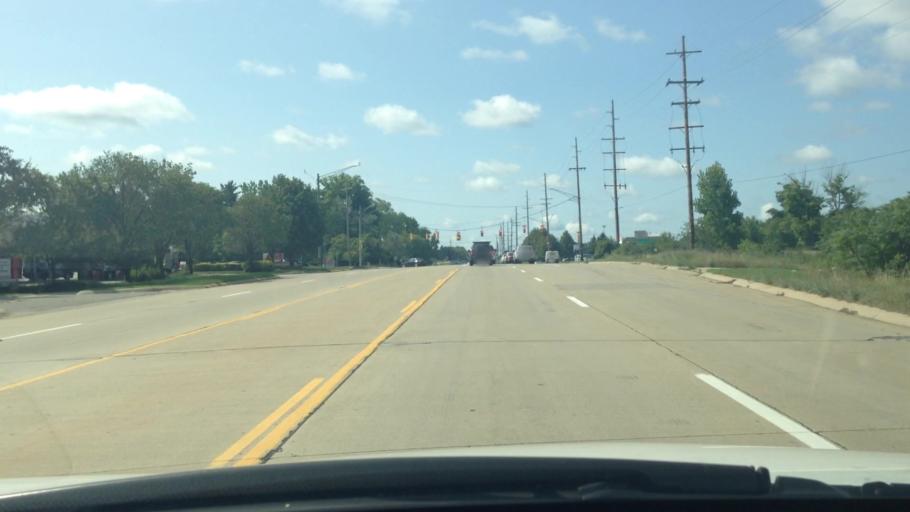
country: US
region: Michigan
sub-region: Oakland County
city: Wolverine Lake
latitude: 42.5618
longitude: -83.4394
